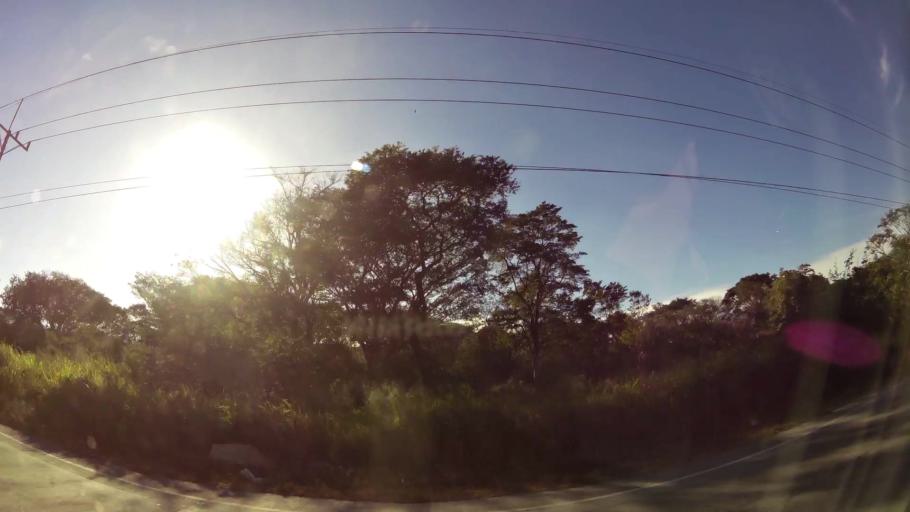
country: SV
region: Santa Ana
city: Metapan
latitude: 14.2720
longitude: -89.4606
